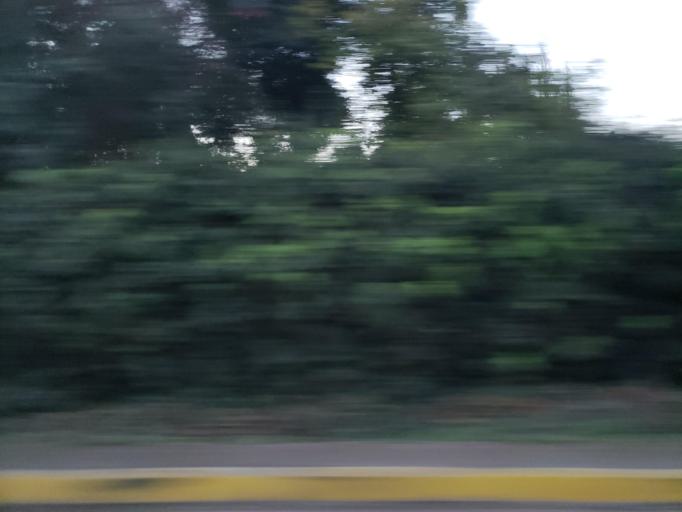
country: CL
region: Santiago Metropolitan
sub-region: Provincia de Talagante
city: El Monte
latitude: -33.6876
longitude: -70.9728
